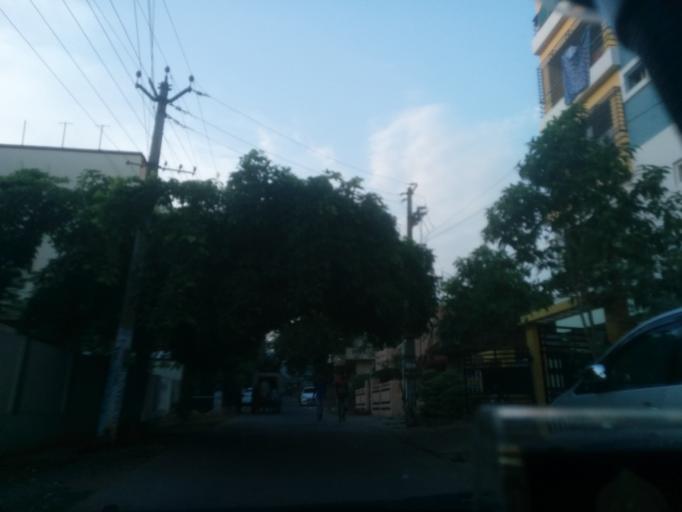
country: IN
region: Andhra Pradesh
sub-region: East Godavari
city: Rajahmundry
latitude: 17.0092
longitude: 81.7970
